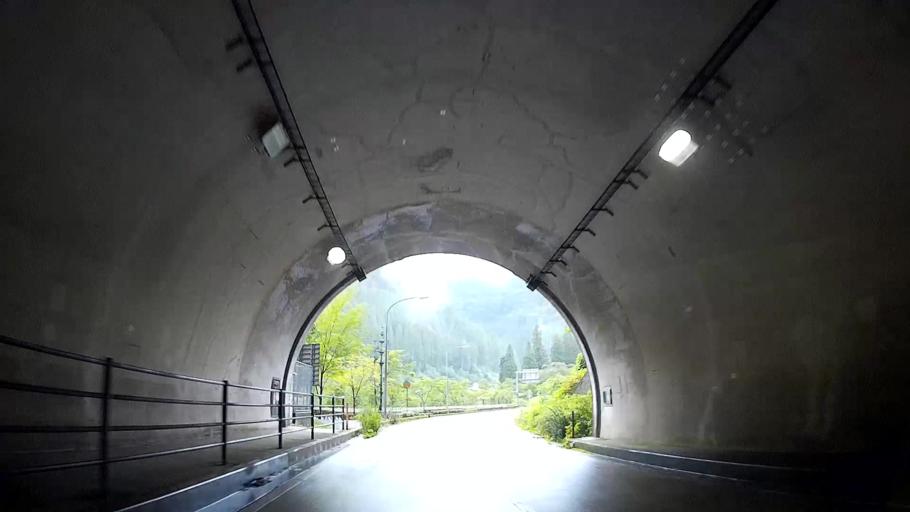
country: JP
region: Oita
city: Tsukawaki
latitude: 33.1803
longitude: 131.0349
